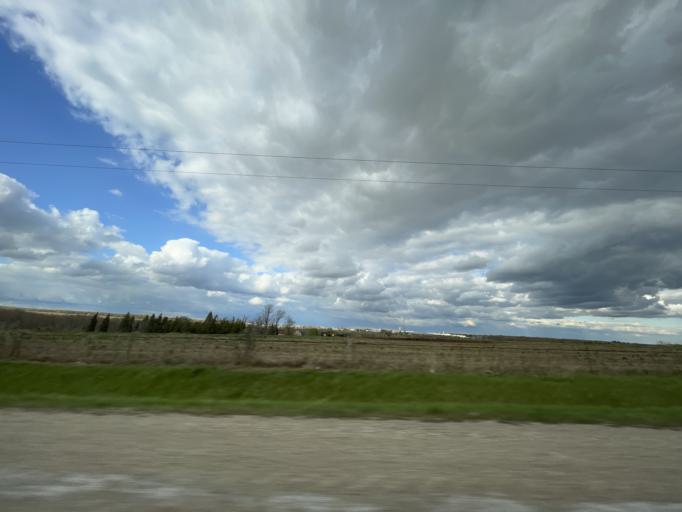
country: CA
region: Ontario
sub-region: Wellington County
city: Guelph
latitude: 43.5239
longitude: -80.3303
